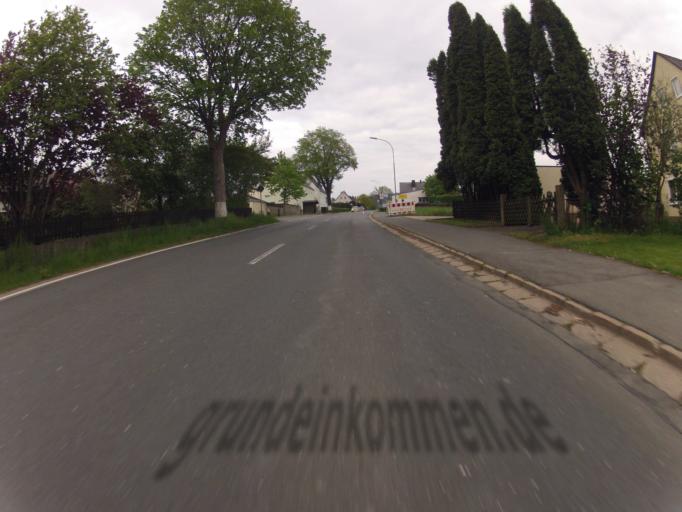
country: DE
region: Bavaria
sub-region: Upper Franconia
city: Sparneck
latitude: 50.1629
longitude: 11.8353
